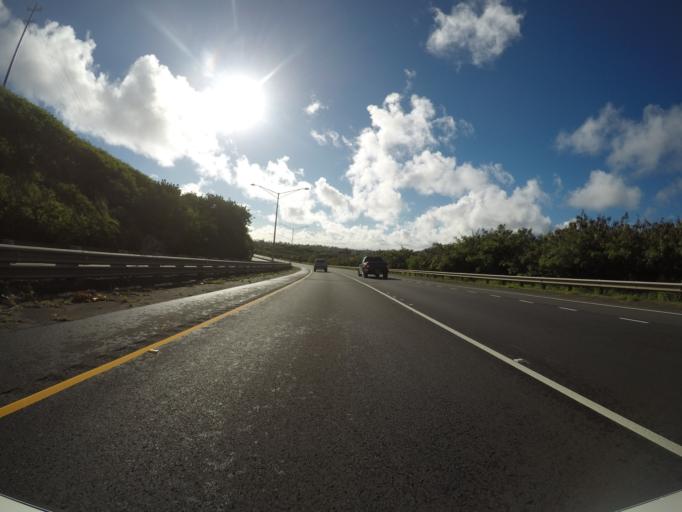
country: US
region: Hawaii
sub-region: Honolulu County
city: Kailua
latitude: 21.4060
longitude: -157.7623
